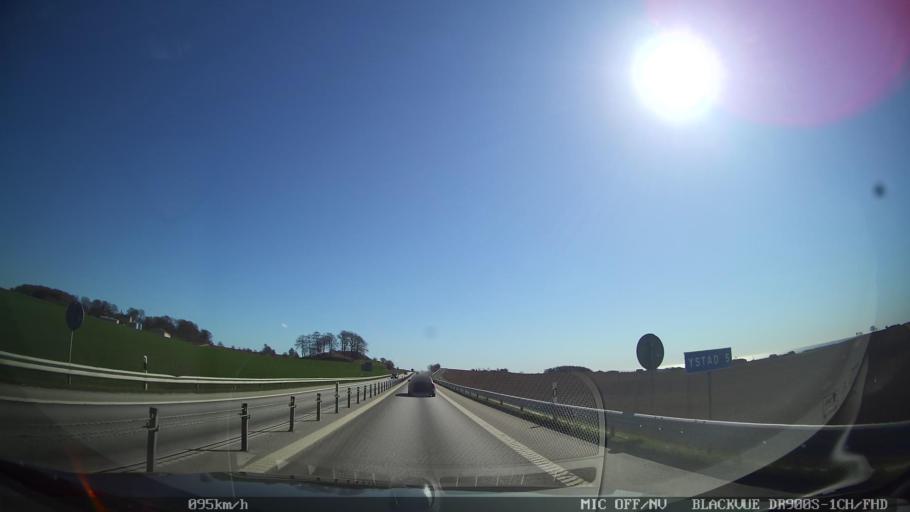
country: SE
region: Skane
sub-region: Ystads Kommun
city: Ystad
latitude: 55.4489
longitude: 13.7674
